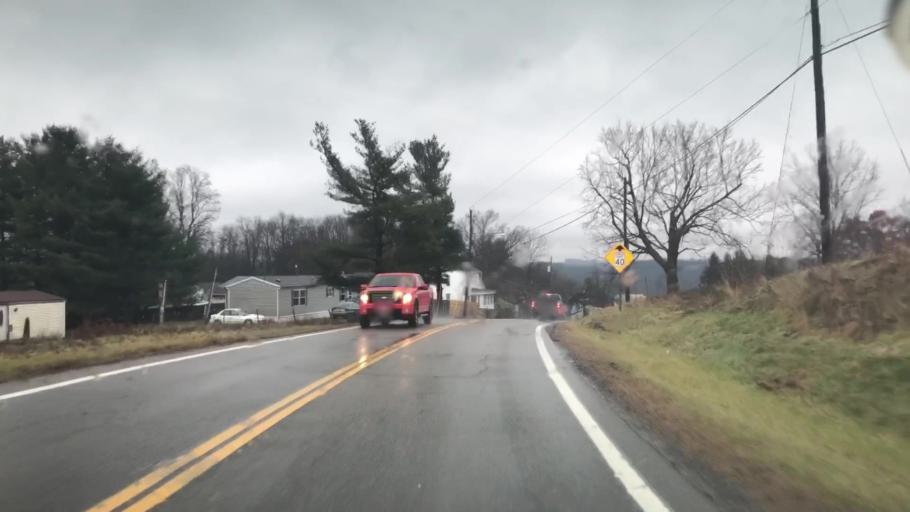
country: US
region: Ohio
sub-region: Belmont County
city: Saint Clairsville
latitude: 40.1302
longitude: -80.9444
